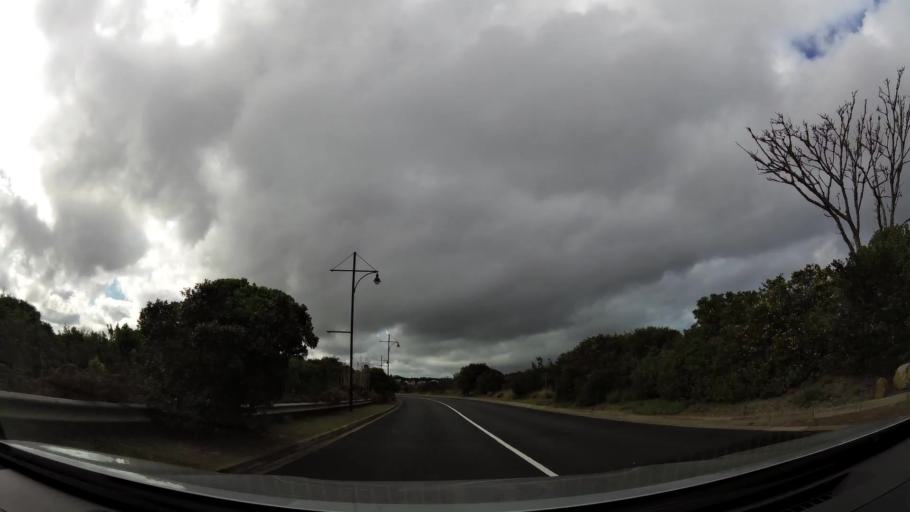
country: ZA
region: Western Cape
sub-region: Eden District Municipality
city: Knysna
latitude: -34.0691
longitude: 23.0906
